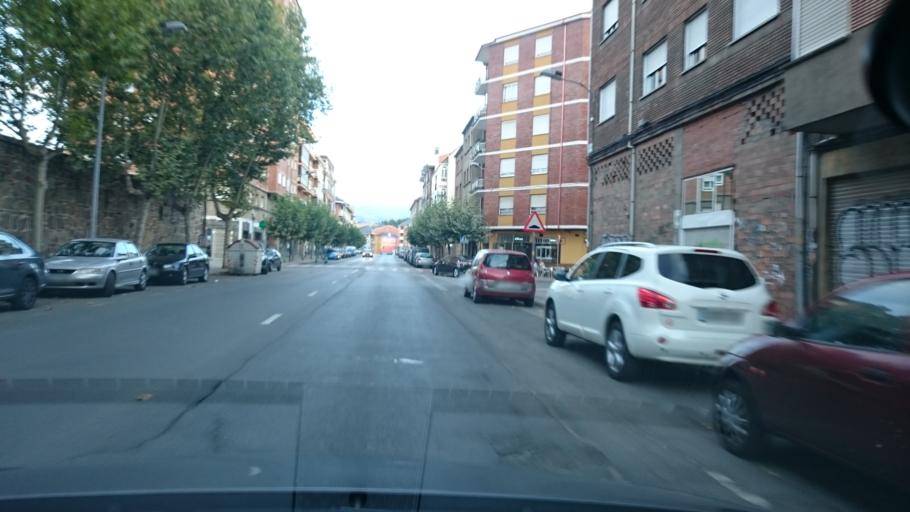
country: ES
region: Castille and Leon
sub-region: Provincia de Leon
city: Ponferrada
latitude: 42.5444
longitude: -6.6017
